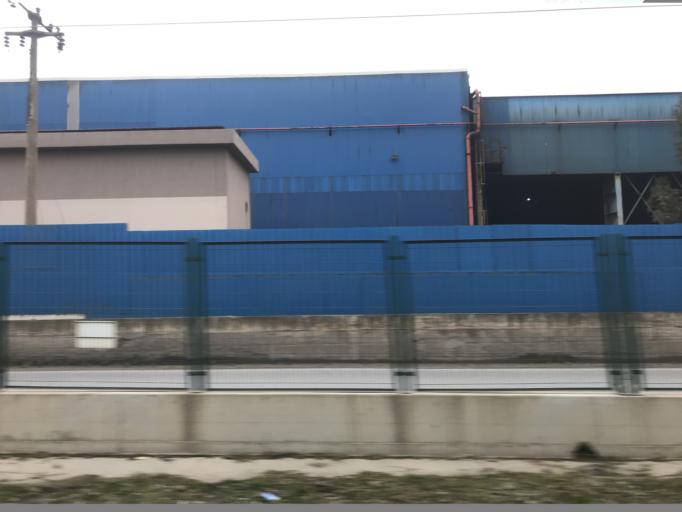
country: TR
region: Kocaeli
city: Darica
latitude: 40.8018
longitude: 29.3759
